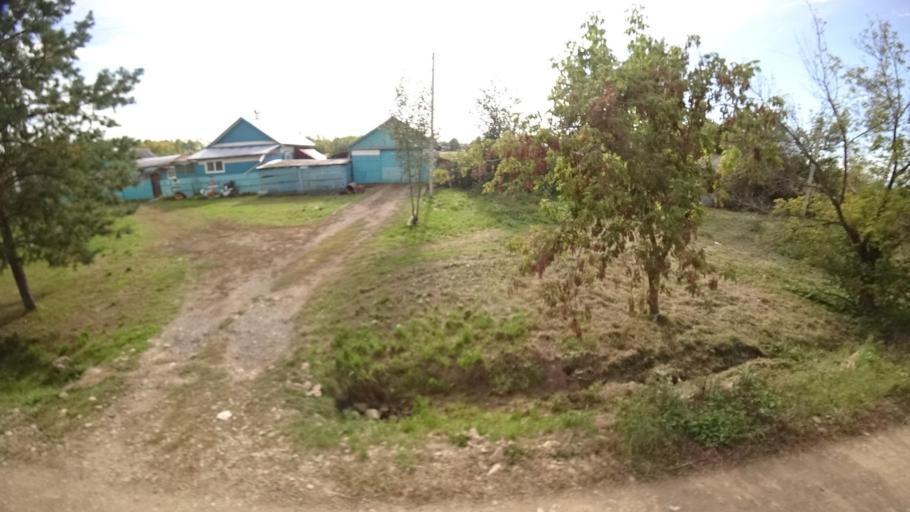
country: RU
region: Primorskiy
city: Dostoyevka
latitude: 44.3028
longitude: 133.4624
